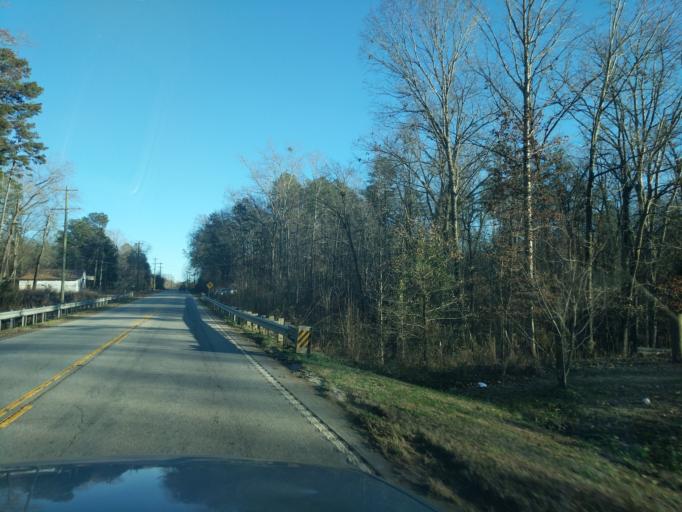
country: US
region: South Carolina
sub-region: Oconee County
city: Westminster
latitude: 34.6895
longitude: -83.1734
